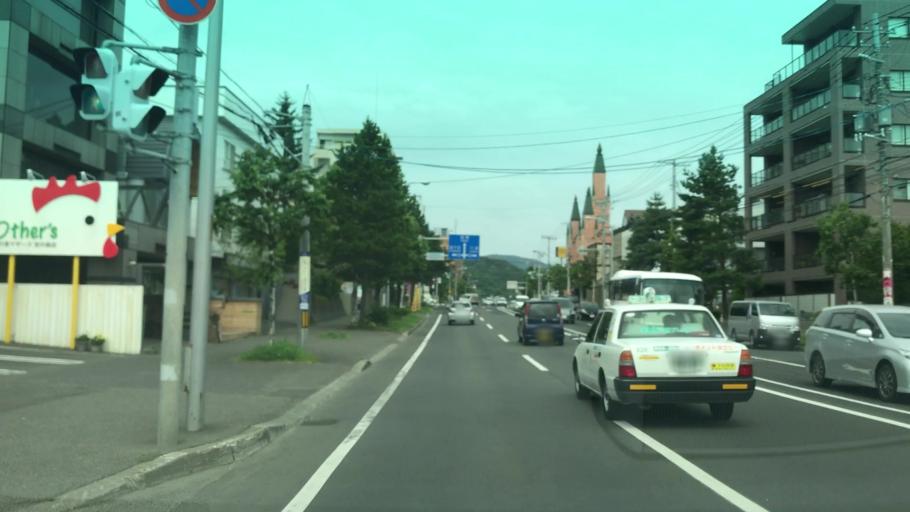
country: JP
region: Hokkaido
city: Sapporo
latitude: 43.0579
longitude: 141.3017
